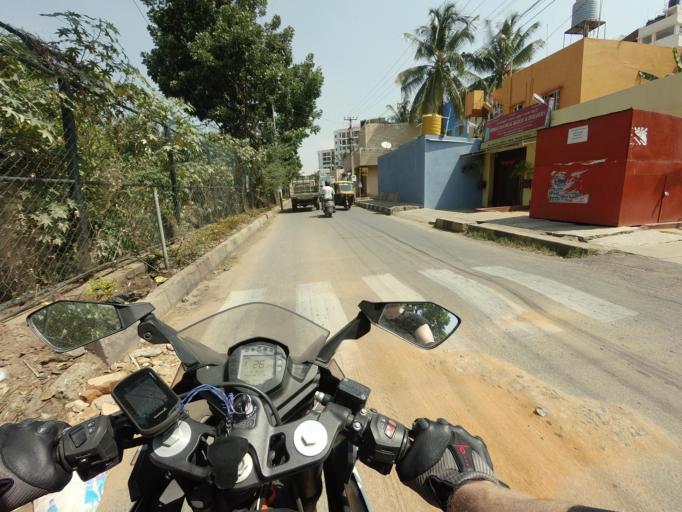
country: IN
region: Karnataka
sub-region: Bangalore Urban
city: Bangalore
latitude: 12.9998
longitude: 77.6614
